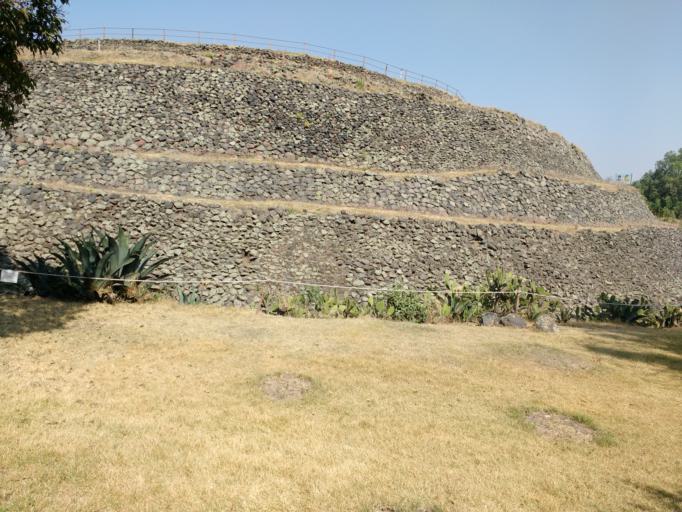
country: MX
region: Mexico City
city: Tlalpan
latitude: 19.3010
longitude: -99.1818
